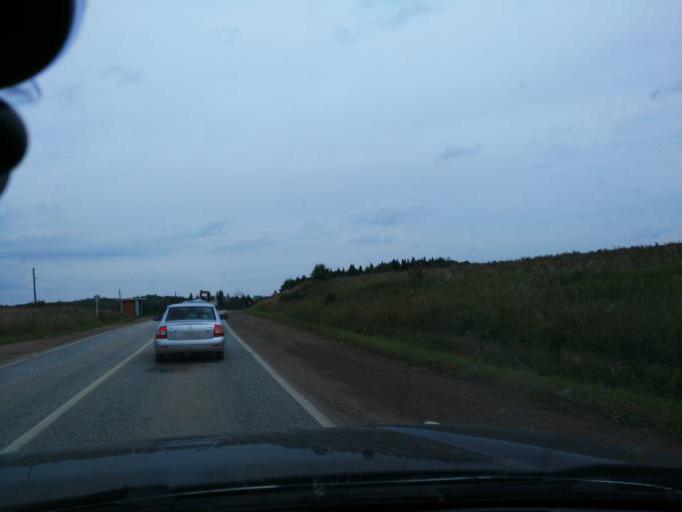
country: RU
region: Perm
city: Chernushka
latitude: 56.5654
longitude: 56.1186
